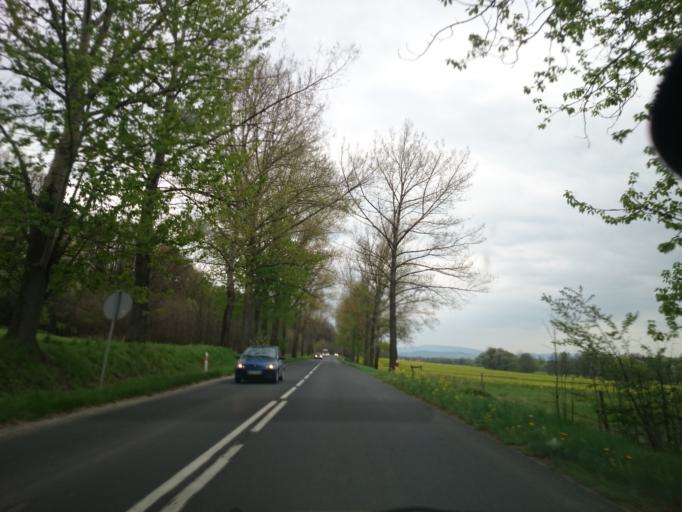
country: PL
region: Opole Voivodeship
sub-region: Powiat nyski
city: Nysa
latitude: 50.4054
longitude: 17.3412
